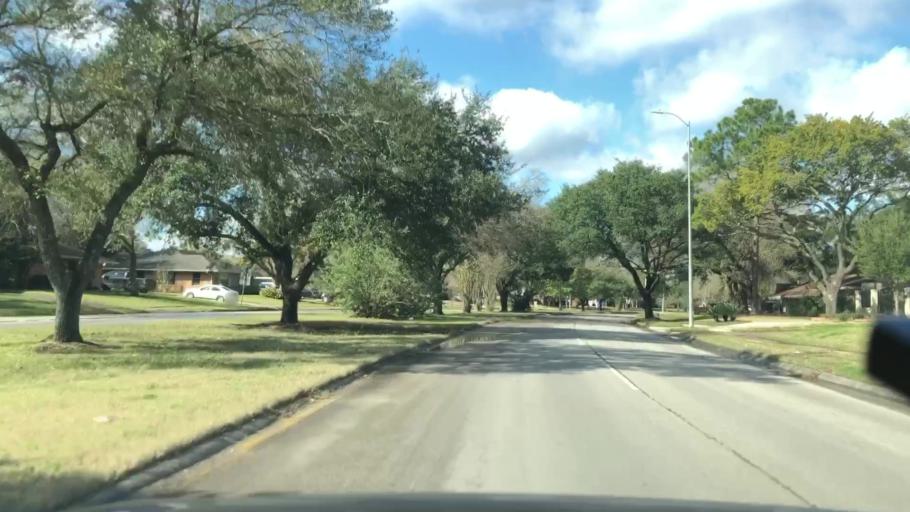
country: US
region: Texas
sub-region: Harris County
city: Bellaire
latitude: 29.6644
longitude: -95.4655
